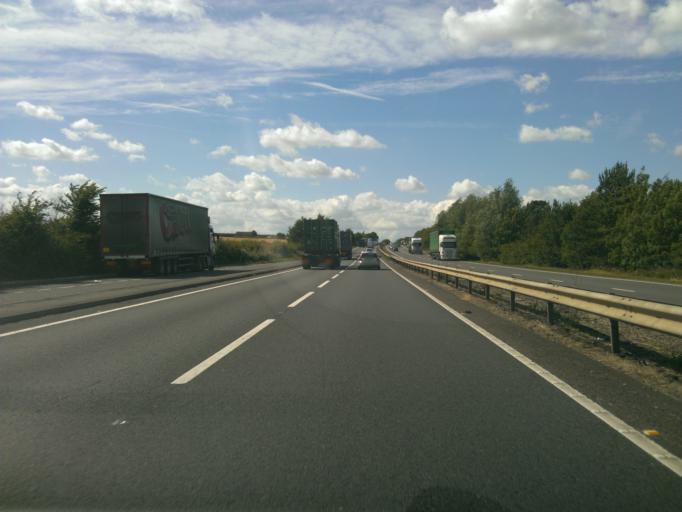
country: GB
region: England
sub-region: Northamptonshire
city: Thrapston
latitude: 52.3889
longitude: -0.5040
